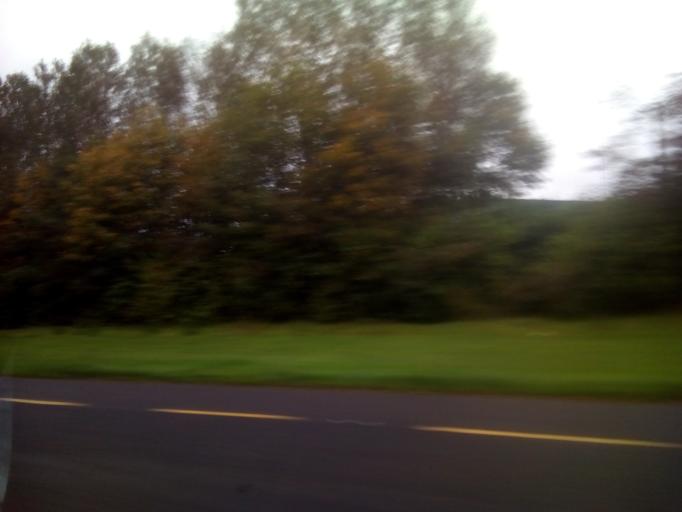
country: IE
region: Leinster
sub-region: An Longfort
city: Longford
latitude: 53.7425
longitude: -7.8056
